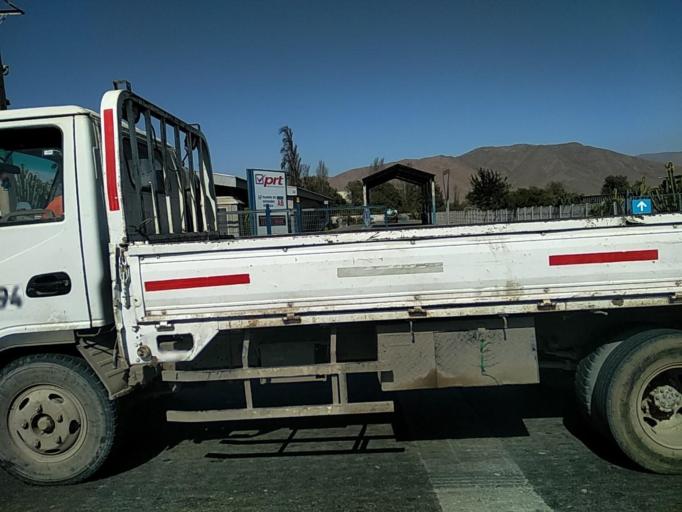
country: CL
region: Atacama
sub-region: Provincia de Copiapo
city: Copiapo
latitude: -27.3922
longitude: -70.3096
